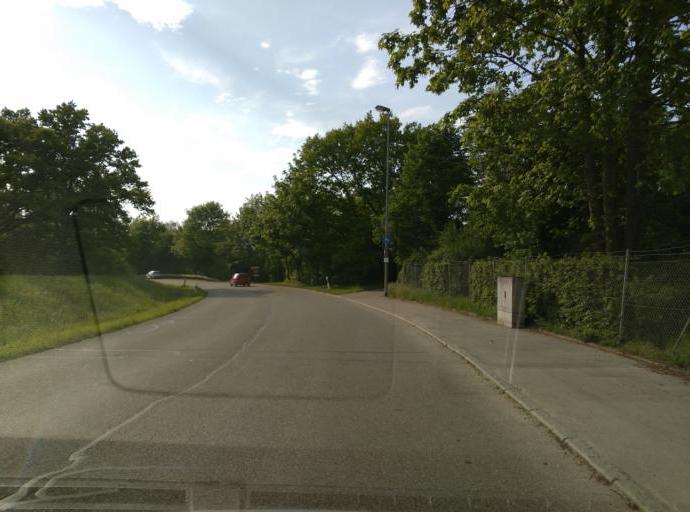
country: DE
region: Baden-Wuerttemberg
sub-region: Tuebingen Region
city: Wannweil
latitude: 48.4961
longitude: 9.1337
